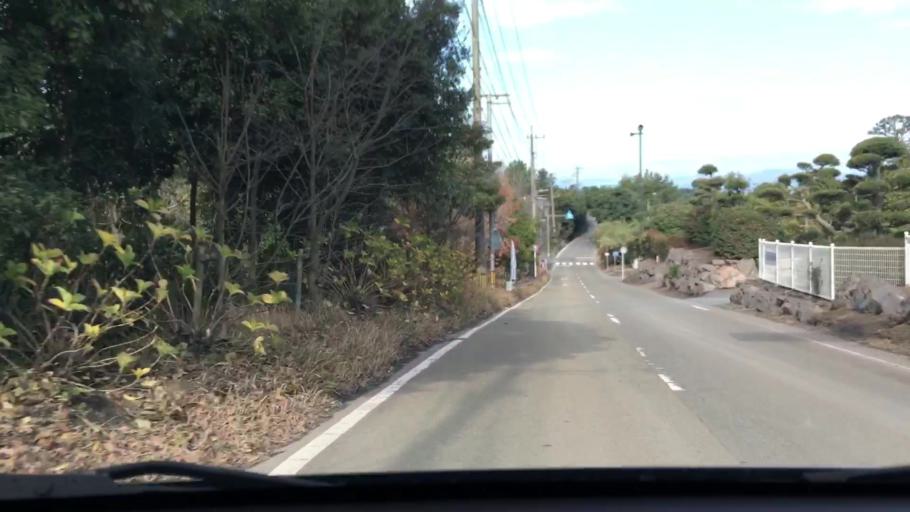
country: JP
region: Kagoshima
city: Hamanoichi
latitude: 31.6134
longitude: 130.7021
